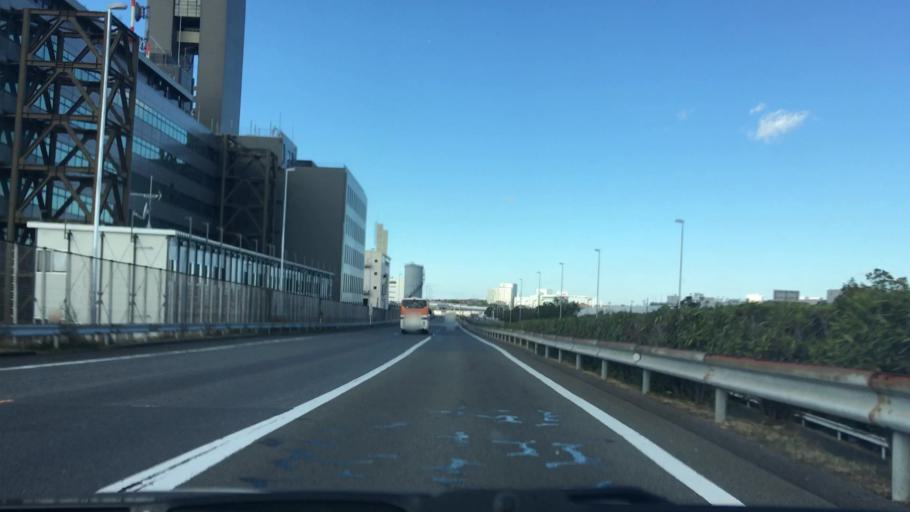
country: JP
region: Chiba
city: Narita
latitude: 35.7691
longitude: 140.3873
